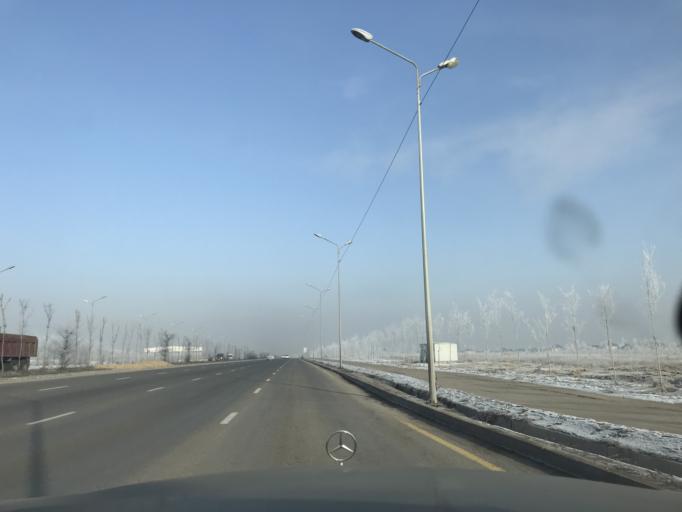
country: KZ
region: Almaty Oblysy
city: Burunday
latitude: 43.3240
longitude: 76.8340
